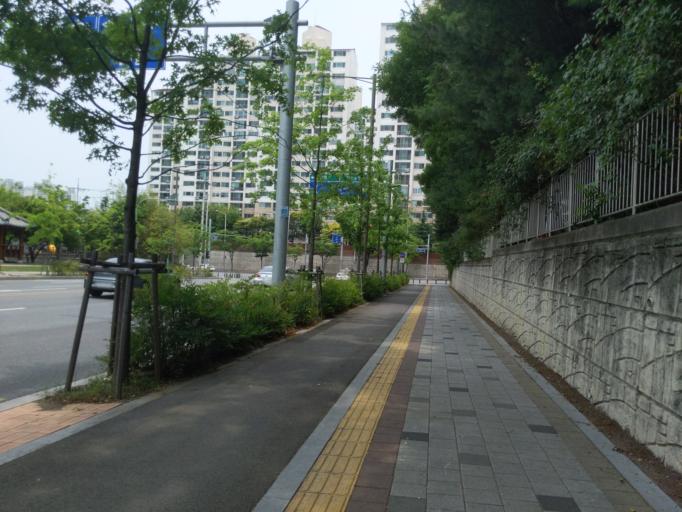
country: KR
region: Daegu
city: Hwawon
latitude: 35.8068
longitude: 128.5284
